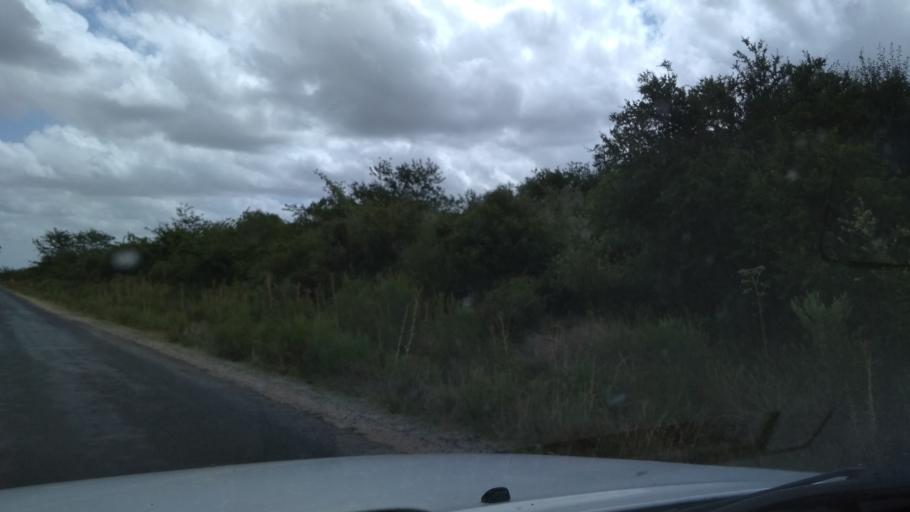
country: UY
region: Canelones
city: San Ramon
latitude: -34.2721
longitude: -55.9451
